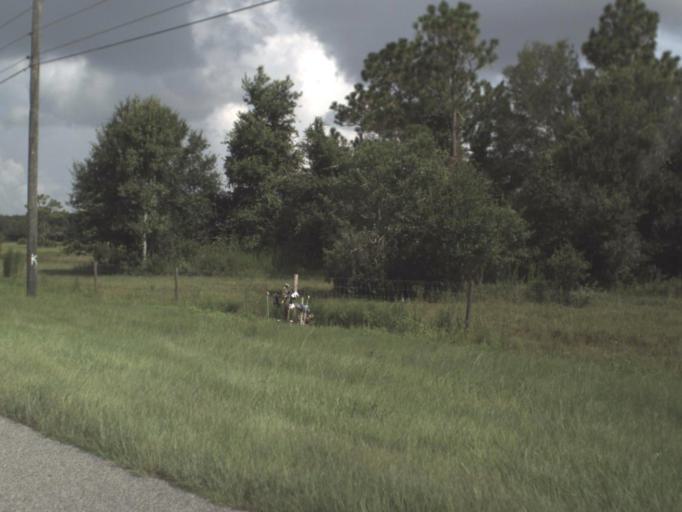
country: US
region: Florida
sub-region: Pasco County
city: Land O' Lakes
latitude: 28.3231
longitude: -82.4599
